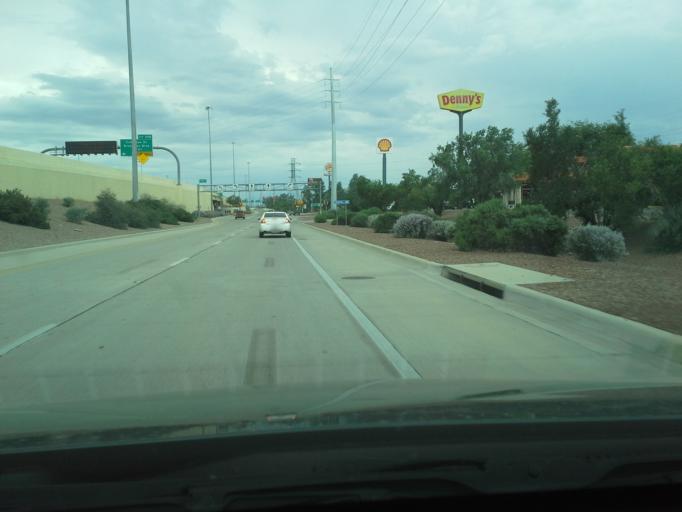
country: US
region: Arizona
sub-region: Pima County
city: South Tucson
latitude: 32.2316
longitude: -110.9836
